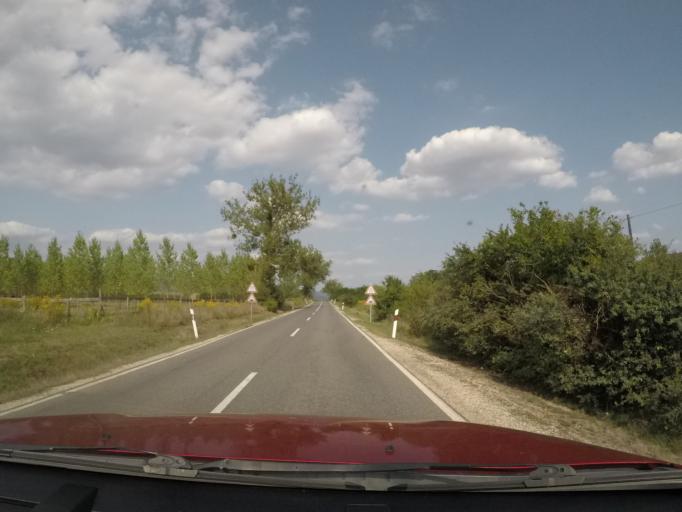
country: HU
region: Borsod-Abauj-Zemplen
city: Szendro
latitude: 48.5223
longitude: 20.7191
